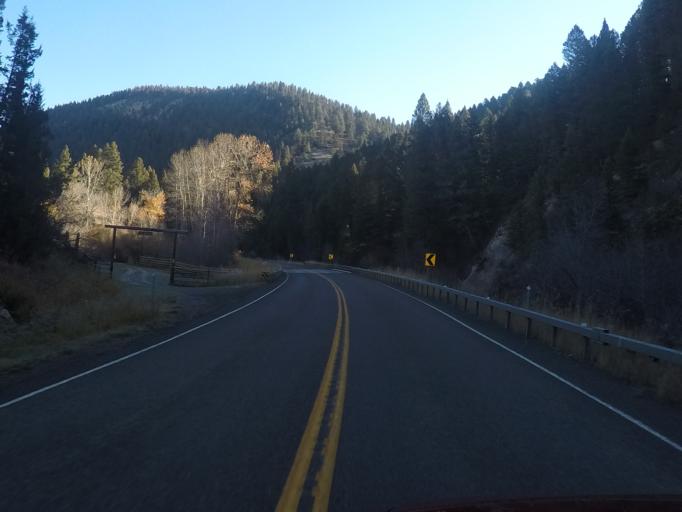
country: US
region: Montana
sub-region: Meagher County
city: White Sulphur Springs
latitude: 46.3483
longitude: -111.1370
